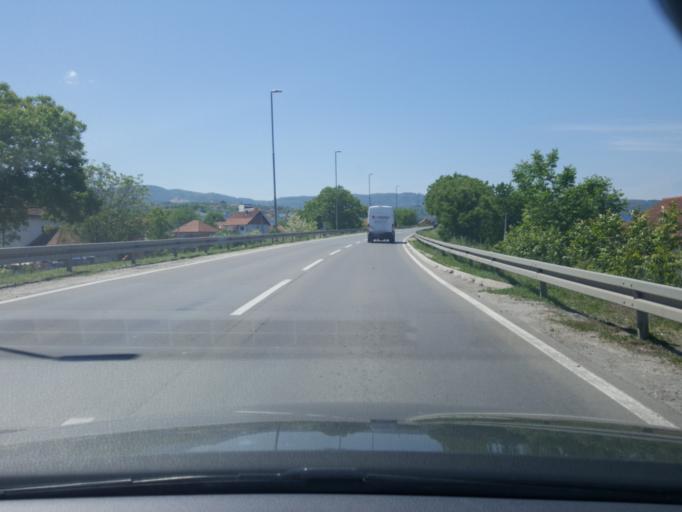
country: RS
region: Central Serbia
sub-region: Moravicki Okrug
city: Cacak
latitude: 43.8795
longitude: 20.3691
